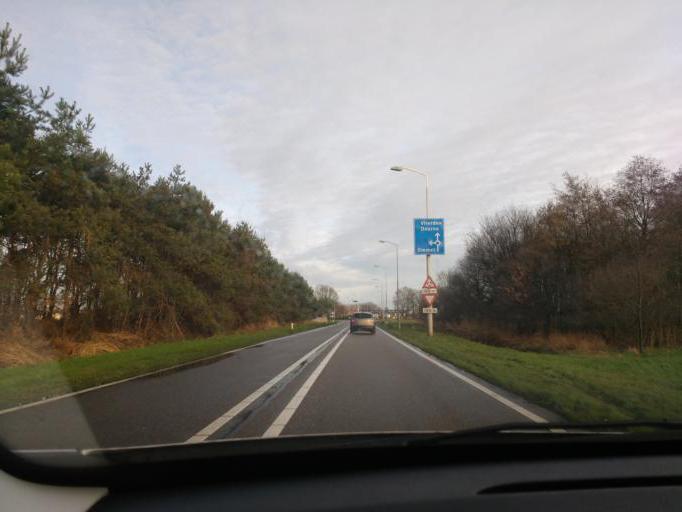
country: NL
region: North Brabant
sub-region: Gemeente Asten
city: Asten
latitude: 51.4273
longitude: 5.7528
